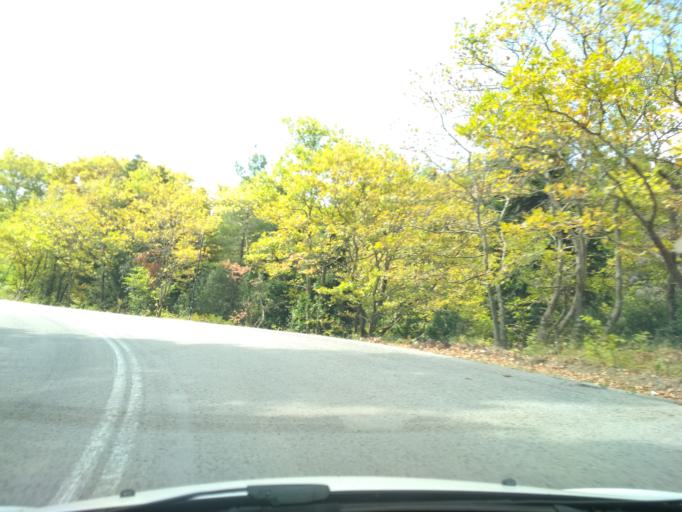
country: GR
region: Central Greece
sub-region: Nomos Evvoias
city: Politika
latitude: 38.6609
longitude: 23.5580
